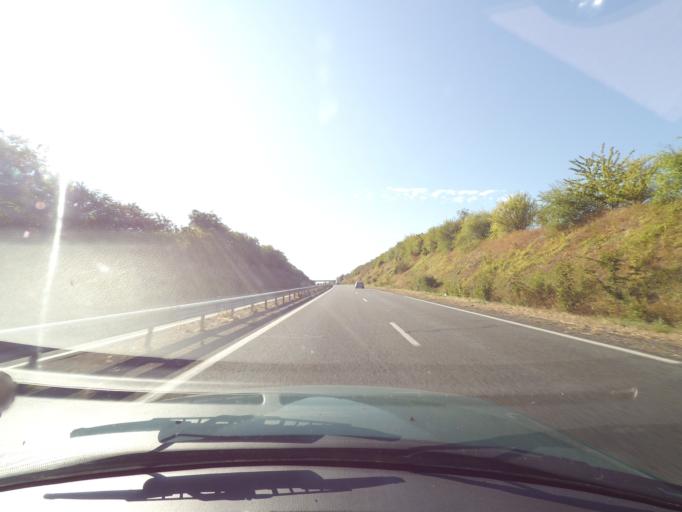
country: FR
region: Poitou-Charentes
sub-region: Departement de la Vienne
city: Migne-Auxances
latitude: 46.6245
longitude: 0.2998
